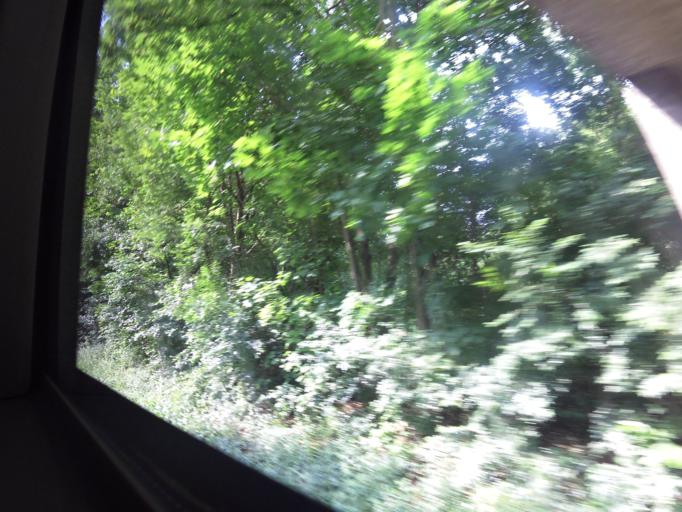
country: DE
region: Bavaria
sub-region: Regierungsbezirk Mittelfranken
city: Nuernberg
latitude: 49.4347
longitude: 11.1020
